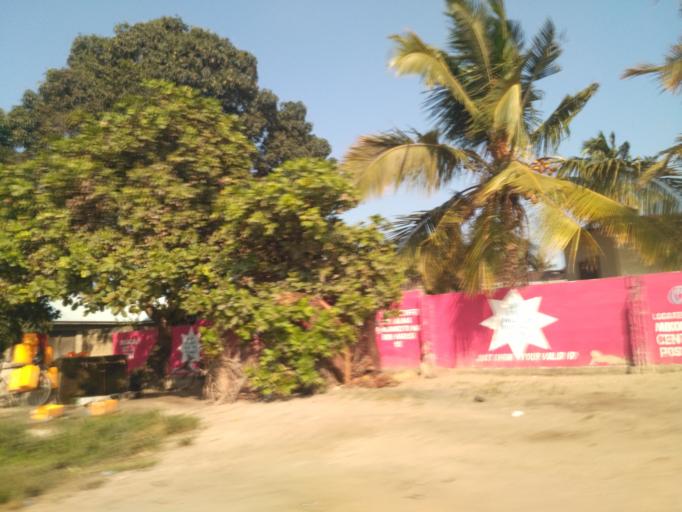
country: TZ
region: Dar es Salaam
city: Dar es Salaam
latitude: -6.8572
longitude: 39.3103
